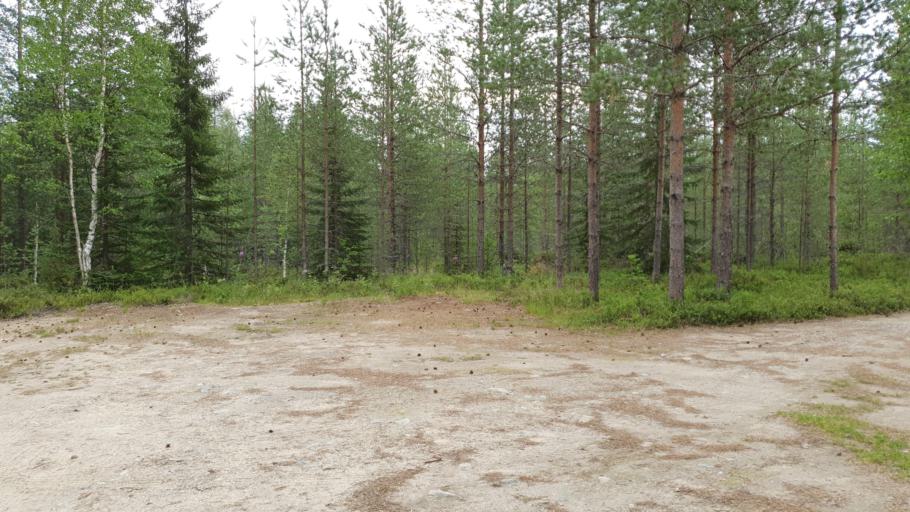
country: FI
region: Kainuu
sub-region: Kehys-Kainuu
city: Kuhmo
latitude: 64.7321
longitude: 29.7161
